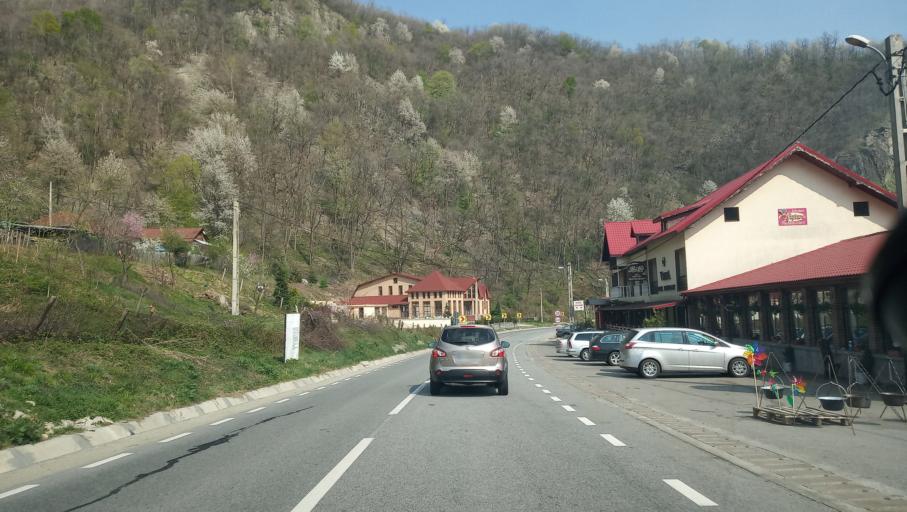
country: RO
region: Gorj
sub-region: Comuna Bumbesti-Jiu
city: Bumbesti-Jiu
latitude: 45.1925
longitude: 23.3880
